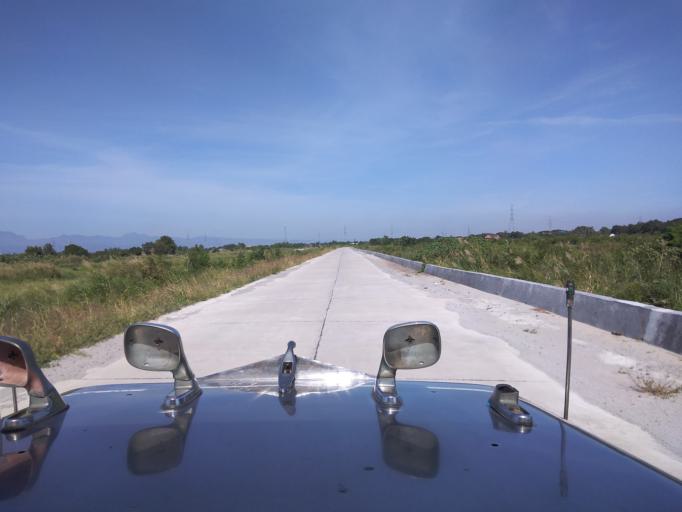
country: PH
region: Central Luzon
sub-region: Province of Pampanga
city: Bacolor
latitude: 14.9983
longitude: 120.6637
